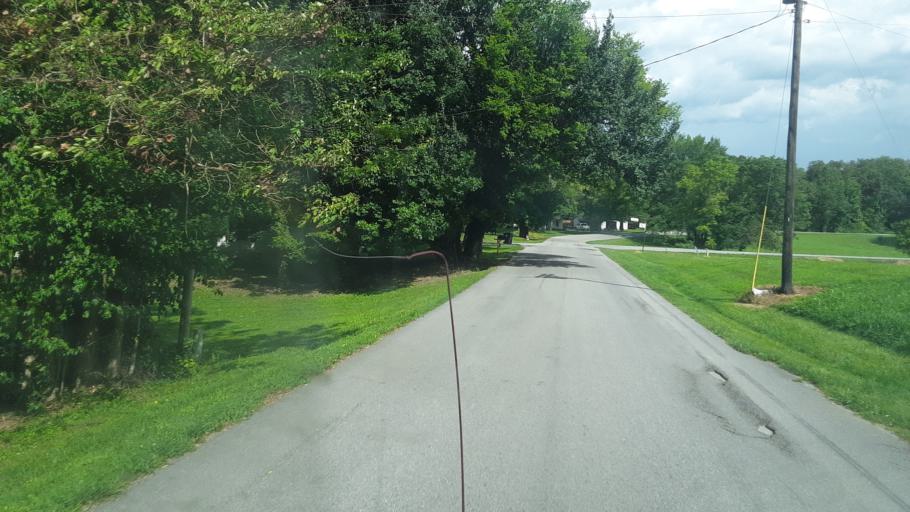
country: US
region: Kentucky
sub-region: Todd County
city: Elkton
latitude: 36.7432
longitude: -87.1664
